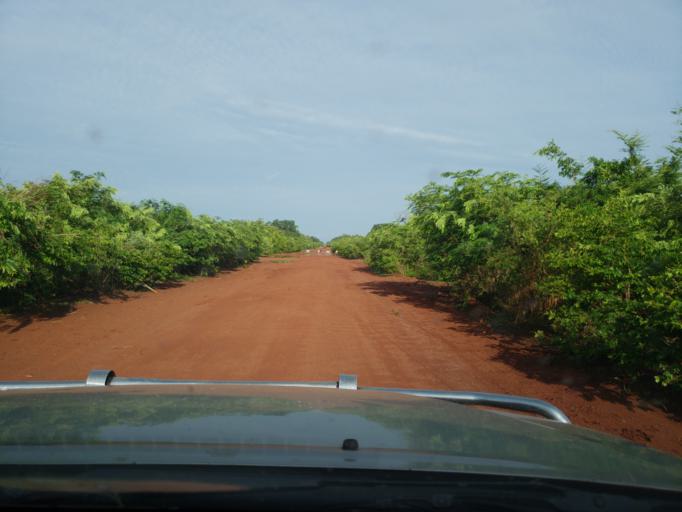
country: ML
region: Sikasso
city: Koutiala
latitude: 12.4177
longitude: -5.7101
